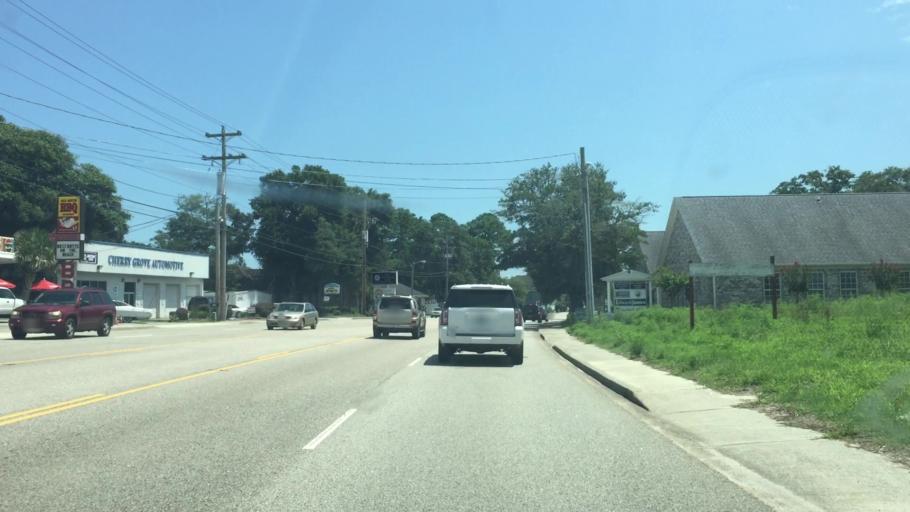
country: US
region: South Carolina
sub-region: Horry County
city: North Myrtle Beach
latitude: 33.8398
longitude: -78.6455
